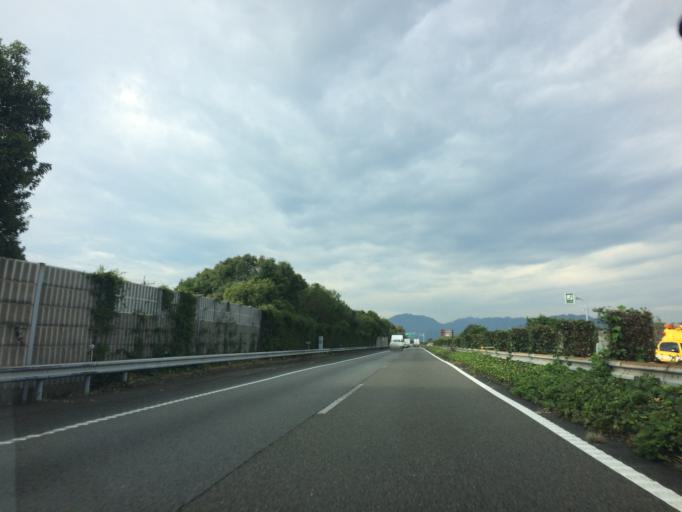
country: JP
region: Shizuoka
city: Shizuoka-shi
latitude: 34.9593
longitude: 138.4188
